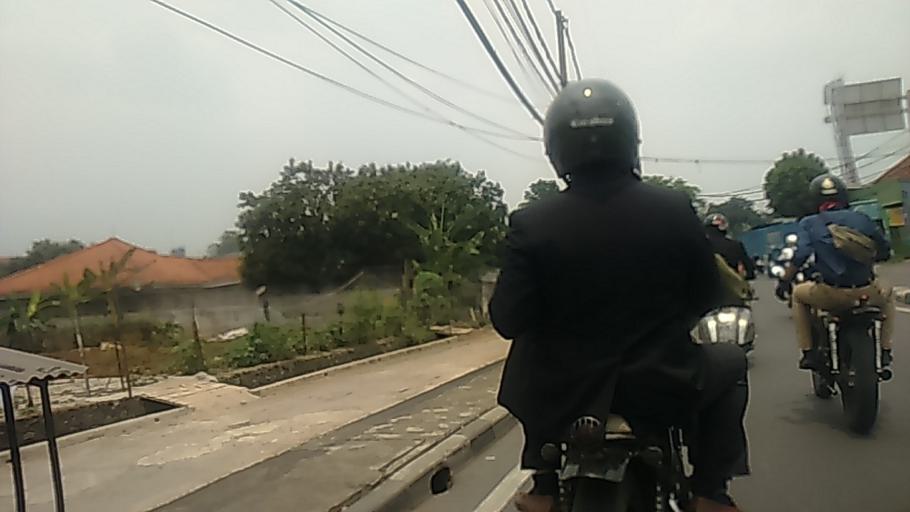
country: ID
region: West Java
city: Pamulang
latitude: -6.2996
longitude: 106.7747
